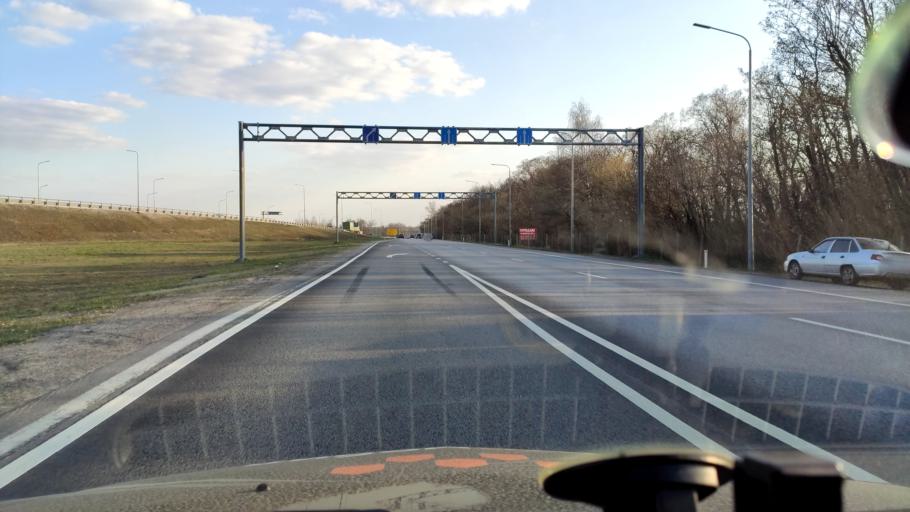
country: RU
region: Voronezj
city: Podgornoye
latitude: 51.8373
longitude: 39.2138
